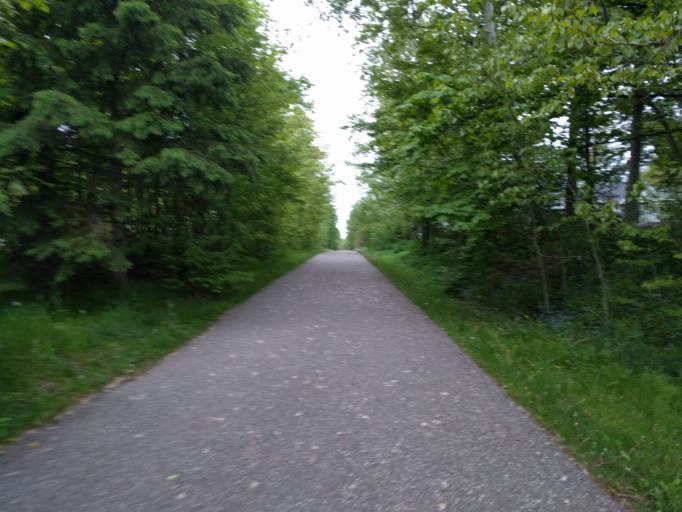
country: US
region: Michigan
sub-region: Marquette County
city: Trowbridge Park
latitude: 46.5494
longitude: -87.4182
